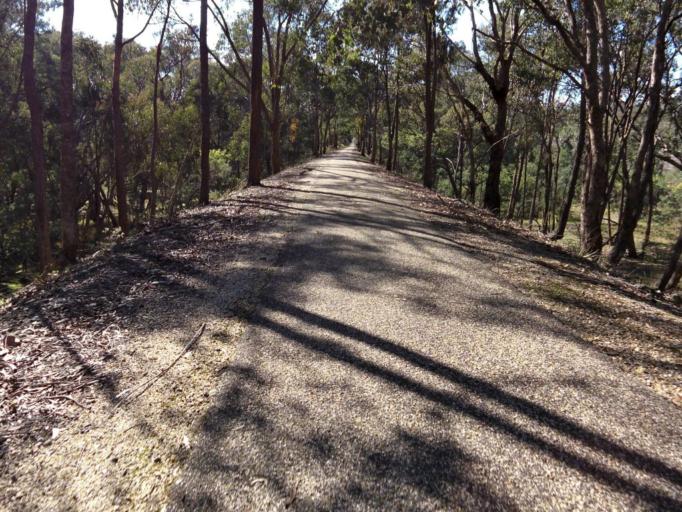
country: AU
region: Victoria
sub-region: Wangaratta
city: Wangaratta
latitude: -36.4058
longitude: 146.6221
